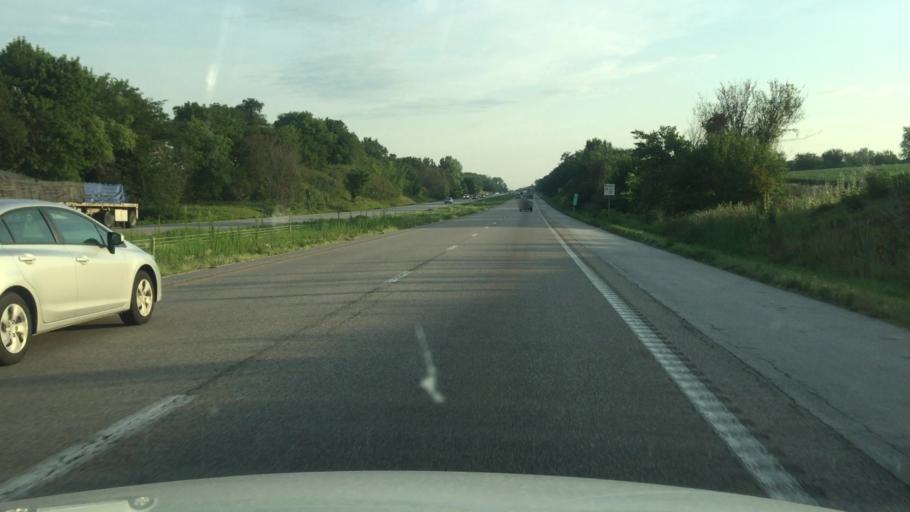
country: US
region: Missouri
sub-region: Platte County
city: Platte City
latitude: 39.4812
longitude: -94.7869
